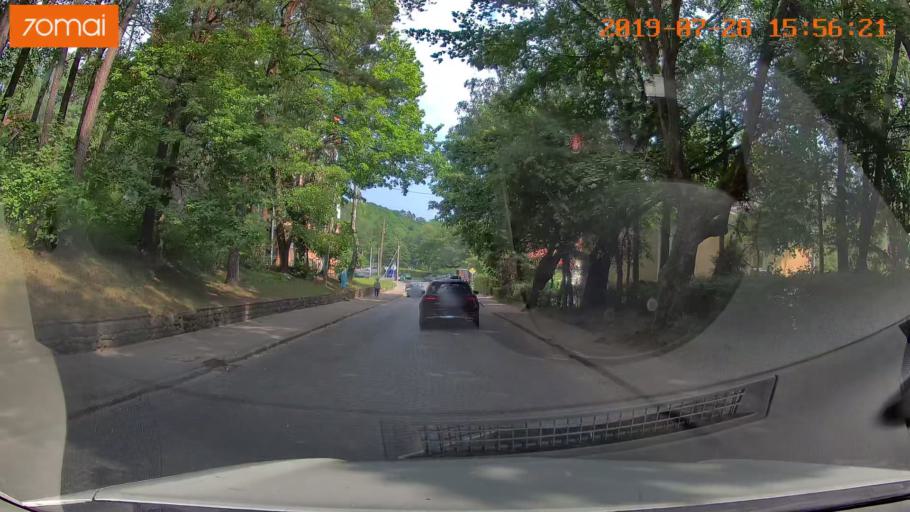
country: RU
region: Kaliningrad
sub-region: Gorod Svetlogorsk
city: Svetlogorsk
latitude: 54.9397
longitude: 20.1463
